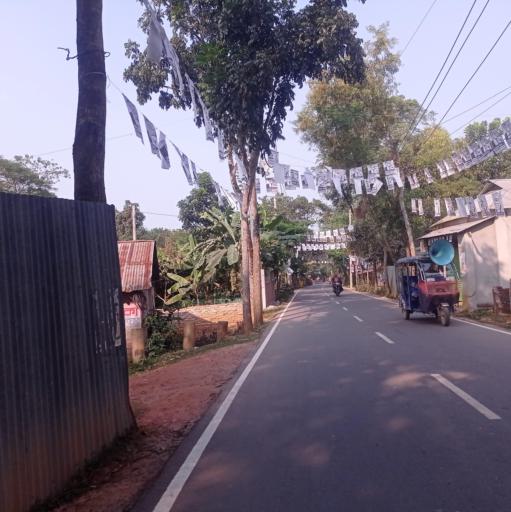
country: BD
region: Dhaka
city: Bhairab Bazar
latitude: 24.0420
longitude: 90.8337
